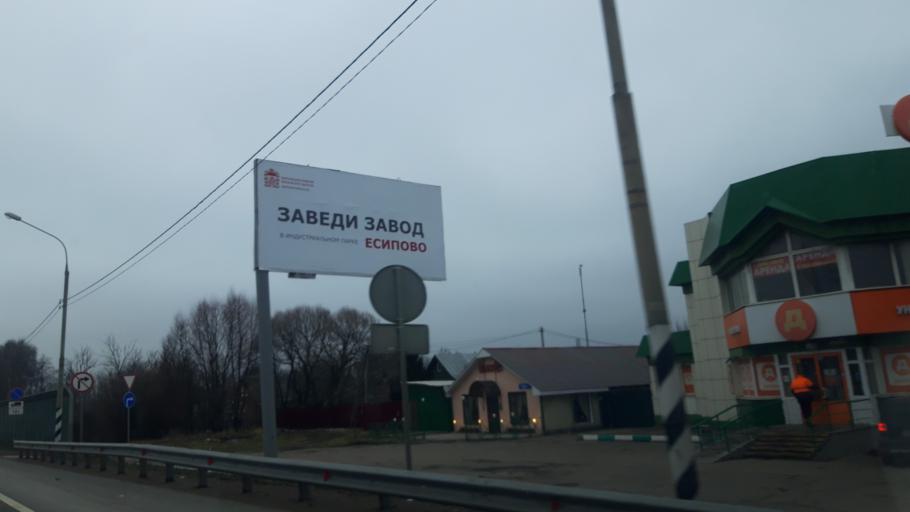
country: RU
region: Moskovskaya
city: Lozhki
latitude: 56.0953
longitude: 37.1069
